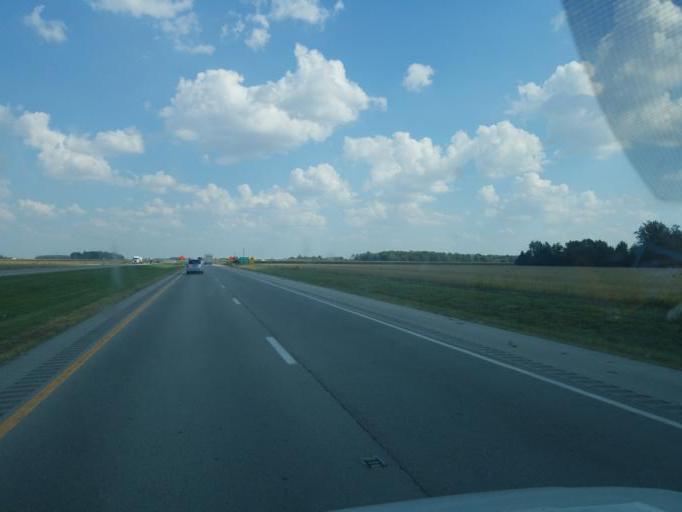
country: US
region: Ohio
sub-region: Van Wert County
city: Van Wert
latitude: 40.8850
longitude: -84.5473
